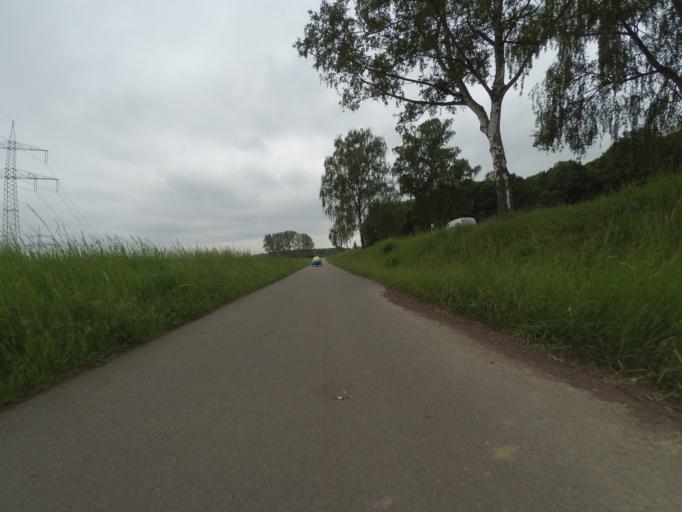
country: DE
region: Lower Saxony
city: Wendeburg
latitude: 52.3482
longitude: 10.3598
